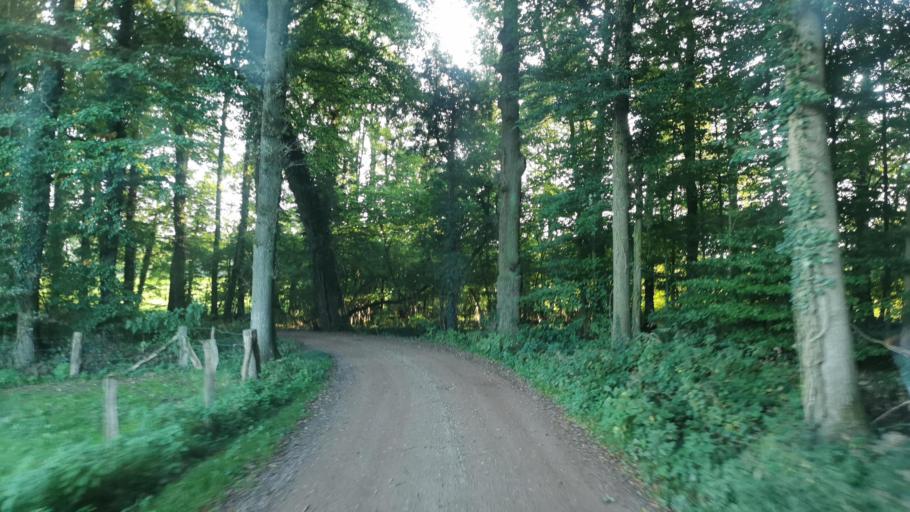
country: NL
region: Overijssel
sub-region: Gemeente Losser
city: Losser
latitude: 52.3045
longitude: 6.9807
